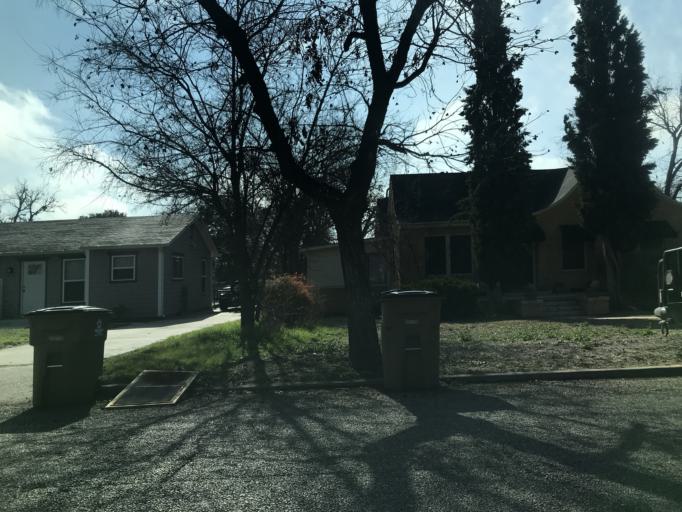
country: US
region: Texas
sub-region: Tom Green County
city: San Angelo
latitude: 31.4531
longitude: -100.4515
